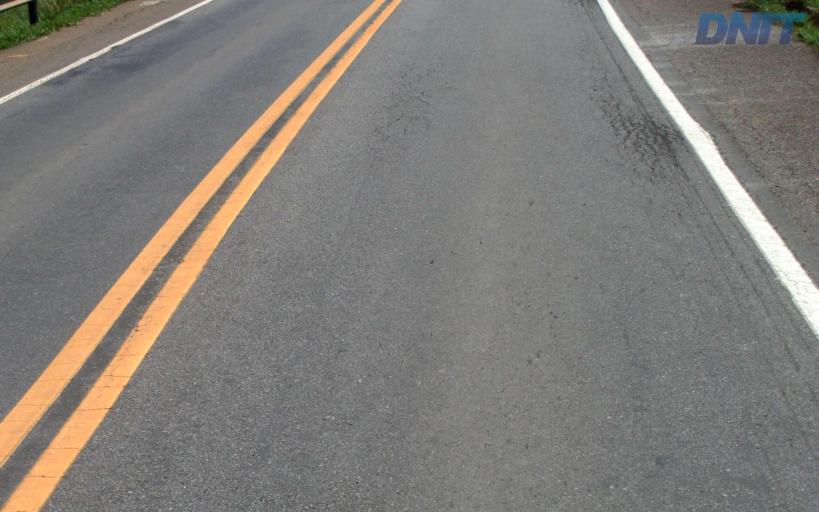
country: BR
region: Minas Gerais
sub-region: Governador Valadares
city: Governador Valadares
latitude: -19.0541
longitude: -42.1602
